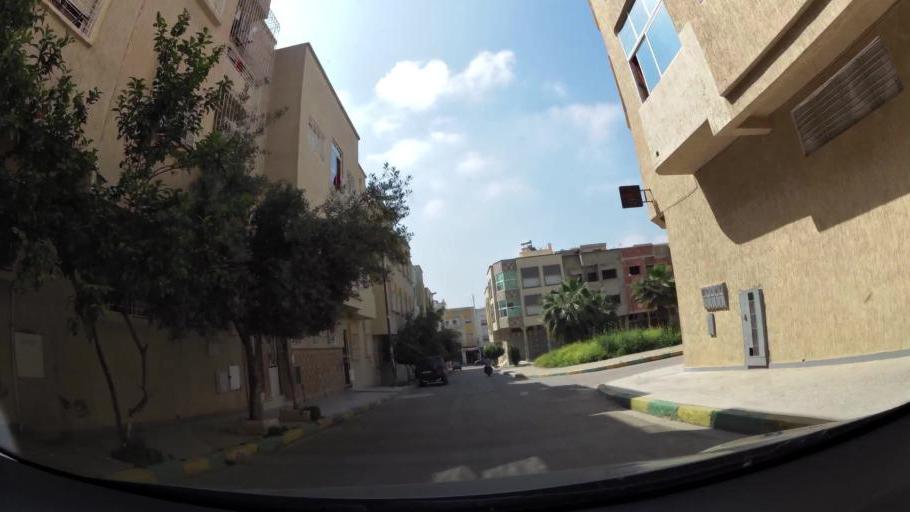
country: MA
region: Fes-Boulemane
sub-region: Fes
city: Fes
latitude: 34.0584
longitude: -5.0245
